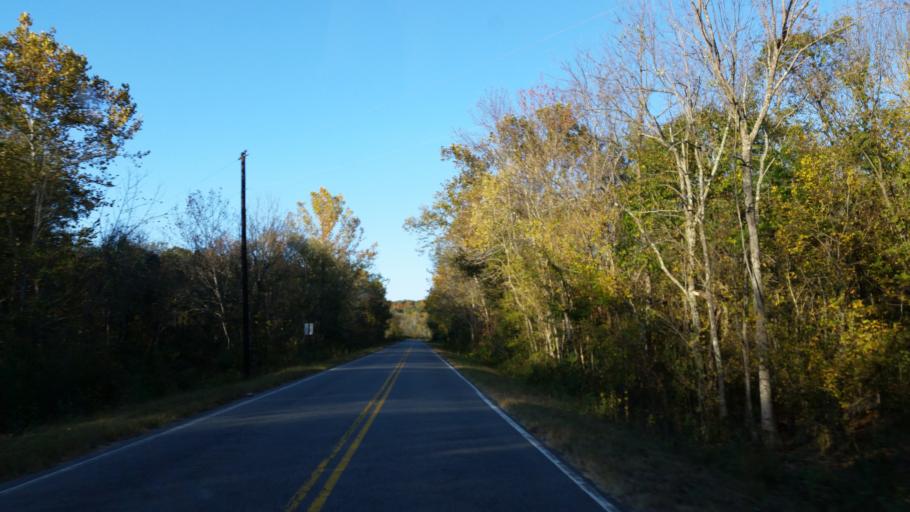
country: US
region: Georgia
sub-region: Bartow County
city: Adairsville
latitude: 34.2707
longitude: -84.9567
